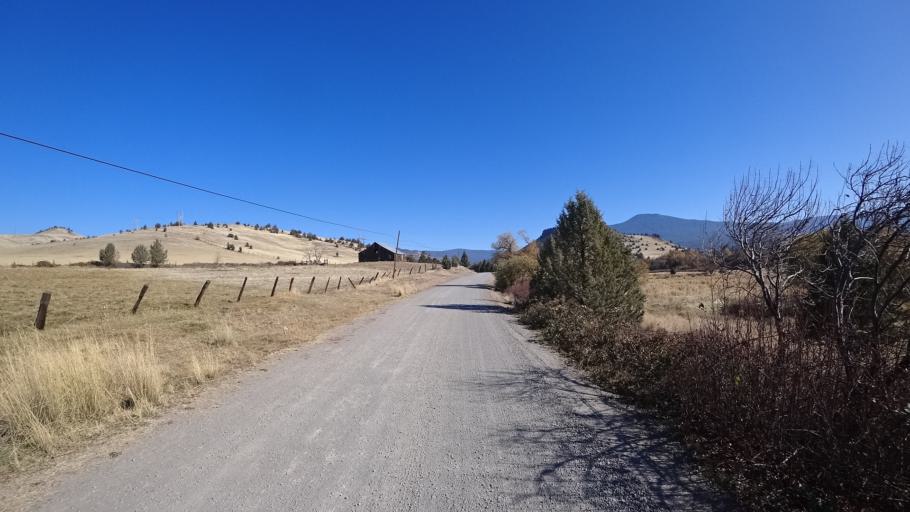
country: US
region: California
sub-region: Siskiyou County
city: Montague
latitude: 41.7293
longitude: -122.3613
